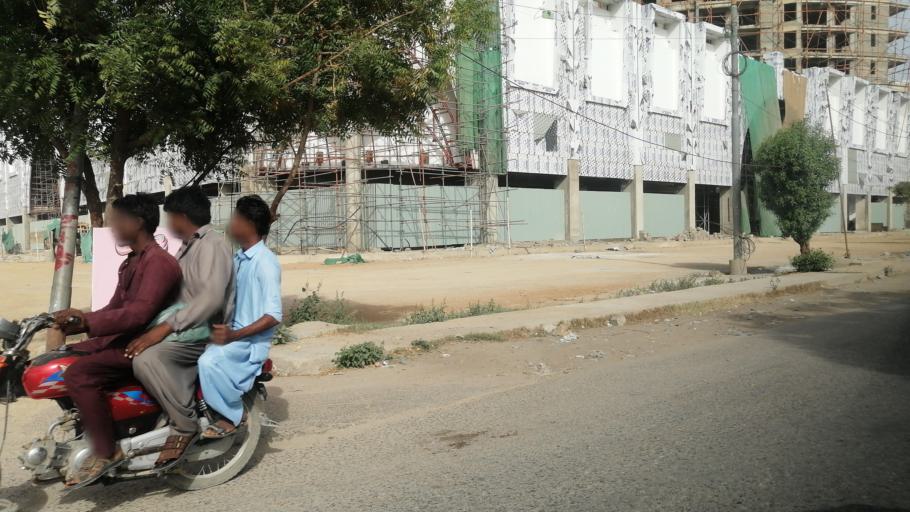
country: PK
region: Sindh
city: Malir Cantonment
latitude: 24.9257
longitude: 67.1800
